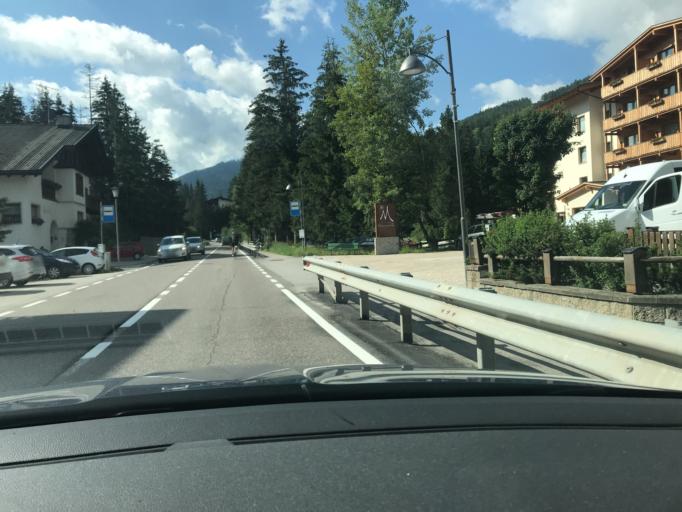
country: IT
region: Trentino-Alto Adige
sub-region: Bolzano
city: Badia
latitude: 46.6042
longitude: 11.8962
